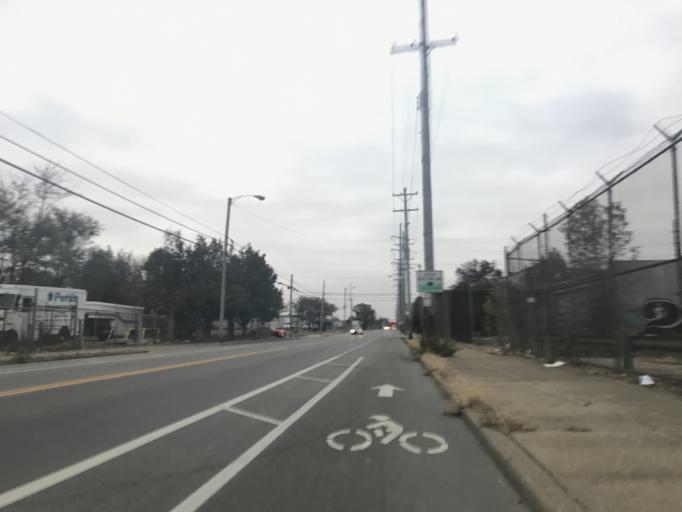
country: US
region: Kentucky
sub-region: Jefferson County
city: Louisville
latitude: 38.2441
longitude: -85.7723
